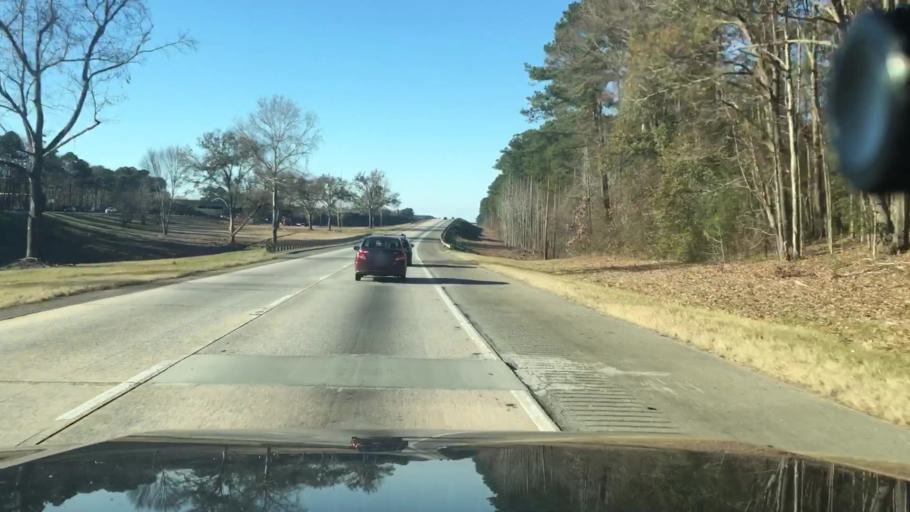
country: US
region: Georgia
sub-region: Monroe County
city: Forsyth
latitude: 32.9546
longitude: -83.8077
